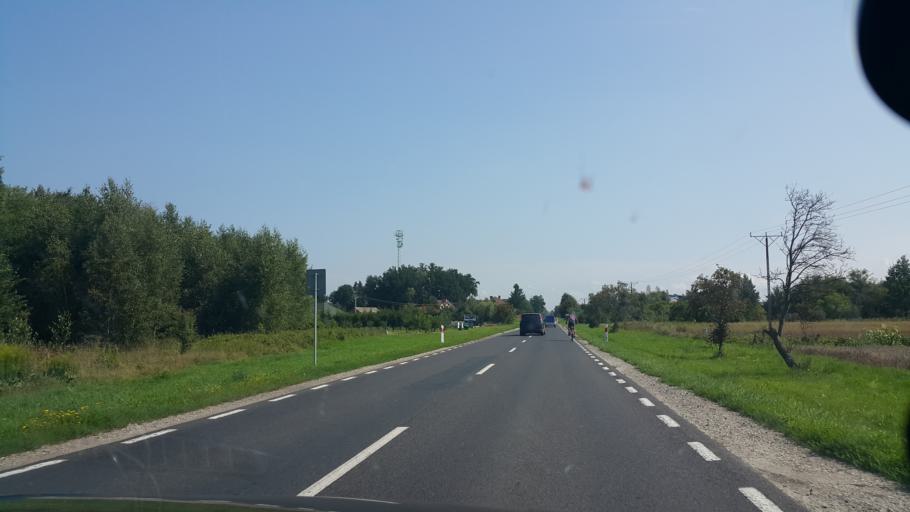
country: PL
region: Lublin Voivodeship
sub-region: Powiat leczynski
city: Cycow
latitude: 51.2989
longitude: 23.1160
